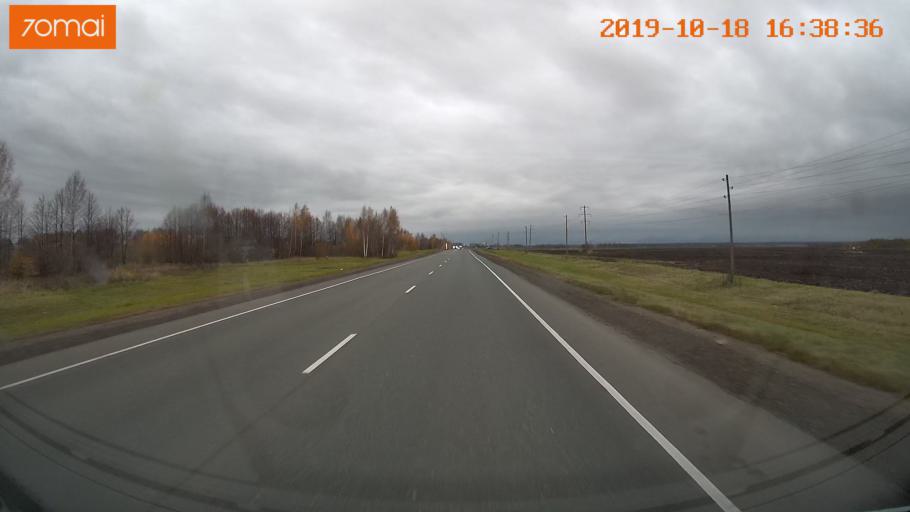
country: RU
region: Vladimir
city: Suzdal'
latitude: 56.4389
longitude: 40.4681
